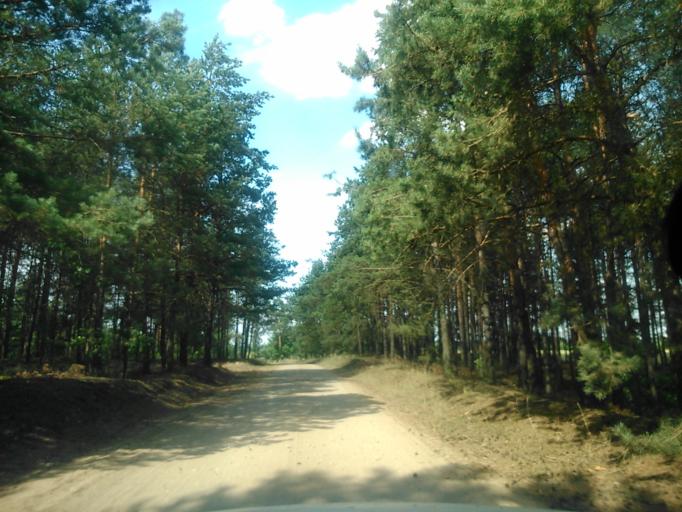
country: PL
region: Masovian Voivodeship
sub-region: Powiat ostrolecki
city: Czarnia
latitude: 53.3833
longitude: 21.2052
